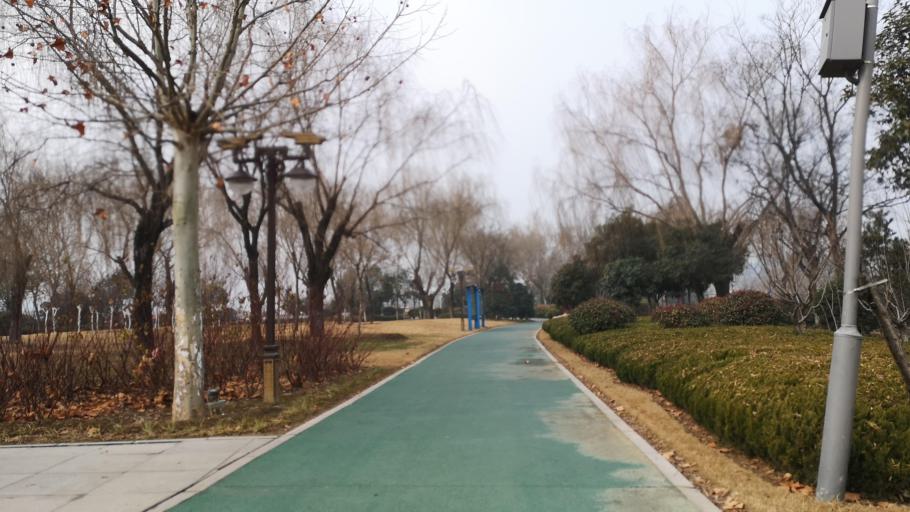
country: CN
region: Henan Sheng
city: Zhongyuanlu
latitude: 35.8009
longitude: 115.0360
